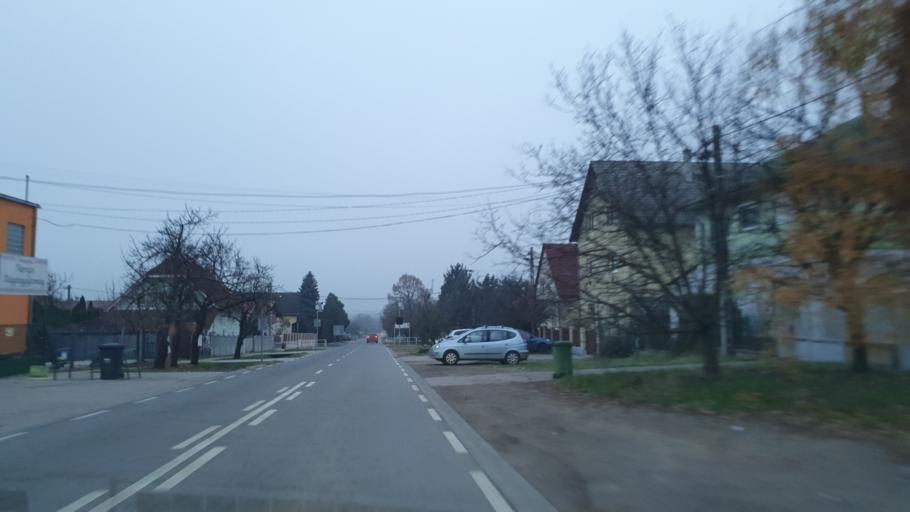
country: HU
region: Pest
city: Csomor
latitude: 47.5401
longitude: 19.2242
